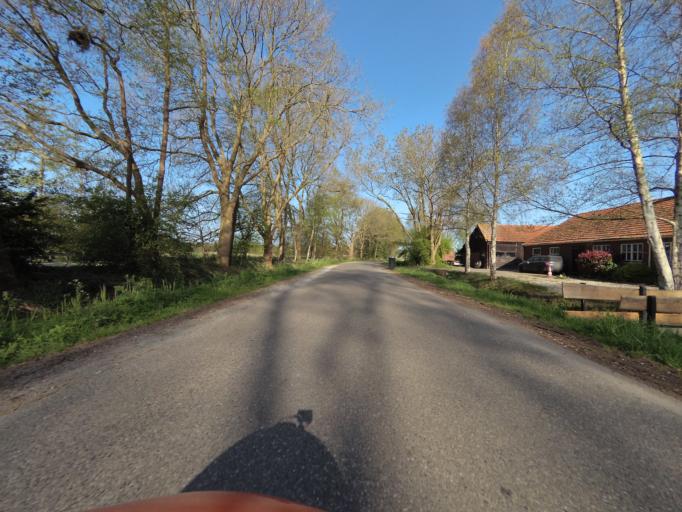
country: NL
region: North Holland
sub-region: Gemeente Naarden
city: Naarden
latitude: 52.2936
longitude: 5.1446
